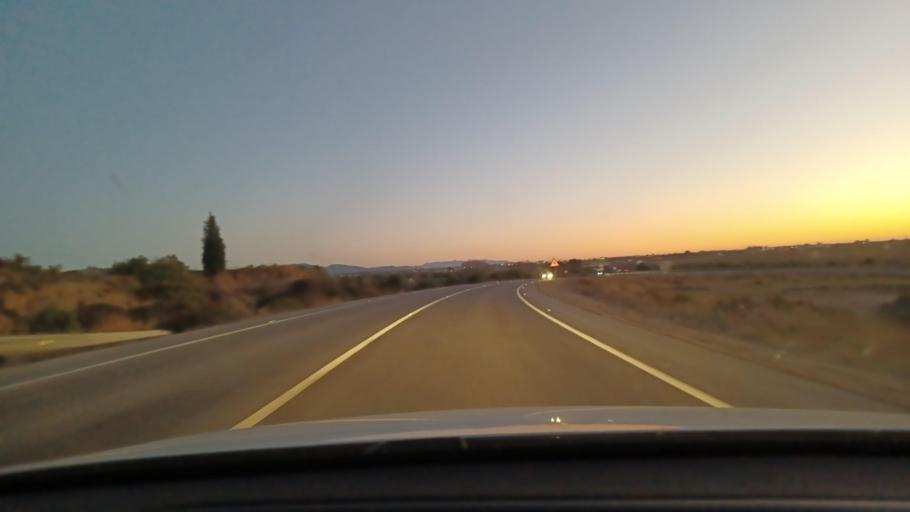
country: ES
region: Catalonia
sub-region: Provincia de Tarragona
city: Amposta
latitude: 40.7342
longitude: 0.5853
